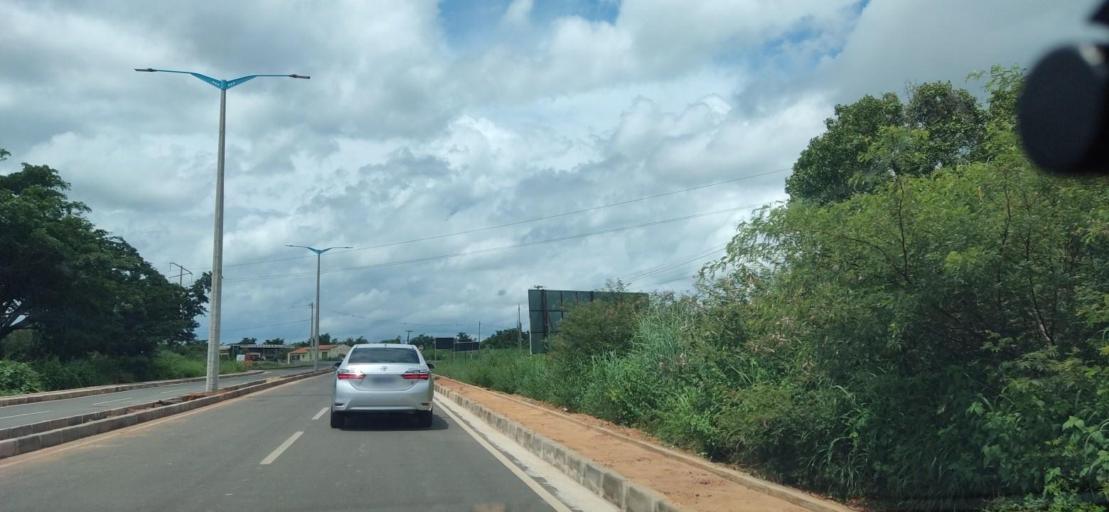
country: BR
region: Piaui
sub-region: Valenca Do Piaui
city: Valenca do Piaui
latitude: -6.4304
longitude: -41.7500
